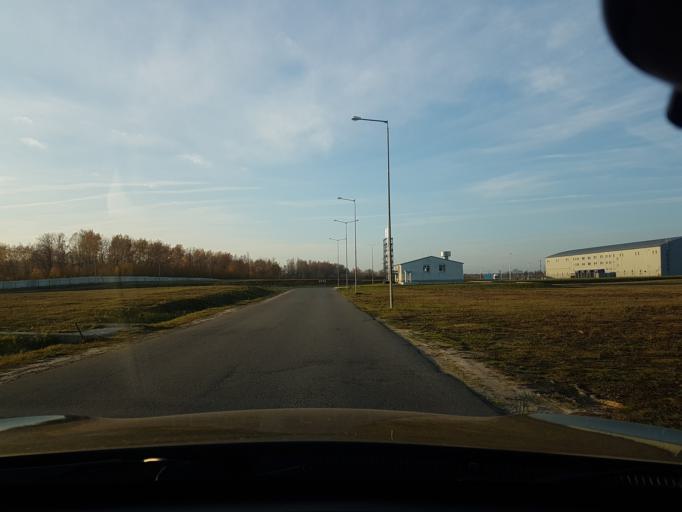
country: BY
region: Minsk
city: Shchomyslitsa
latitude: 53.8225
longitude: 27.4334
